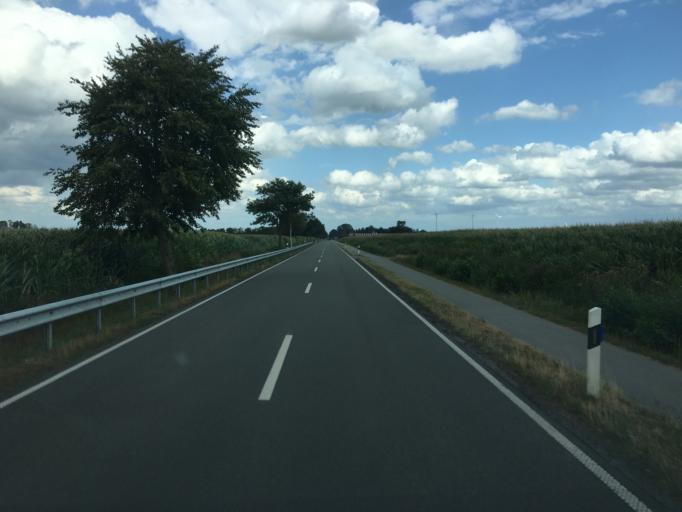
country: DE
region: Lower Saxony
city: Barssel
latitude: 53.0773
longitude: 7.7472
